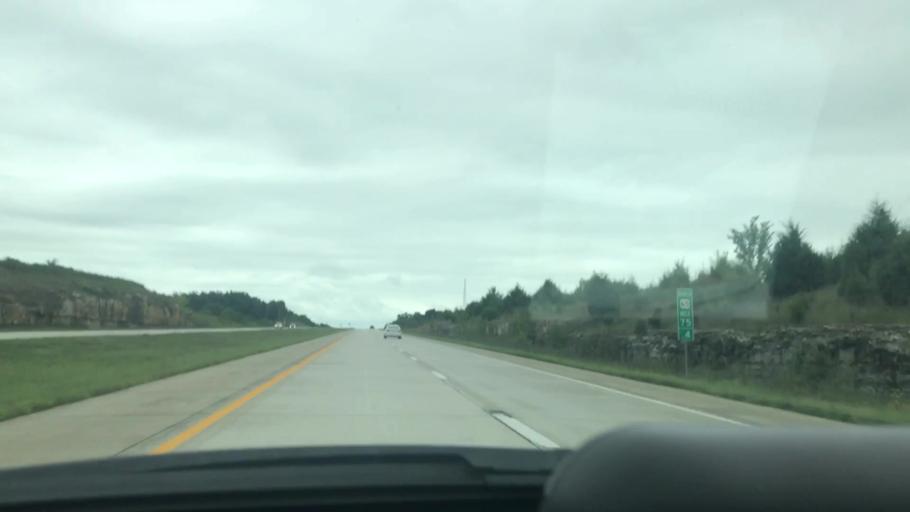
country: US
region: Missouri
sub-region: Dallas County
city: Buffalo
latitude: 37.5349
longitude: -93.1372
